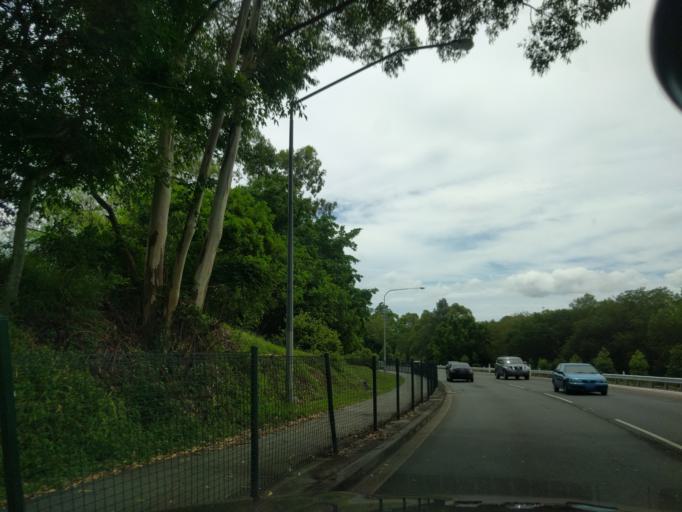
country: AU
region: Queensland
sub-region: Brisbane
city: Stafford
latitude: -27.4135
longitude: 153.0055
